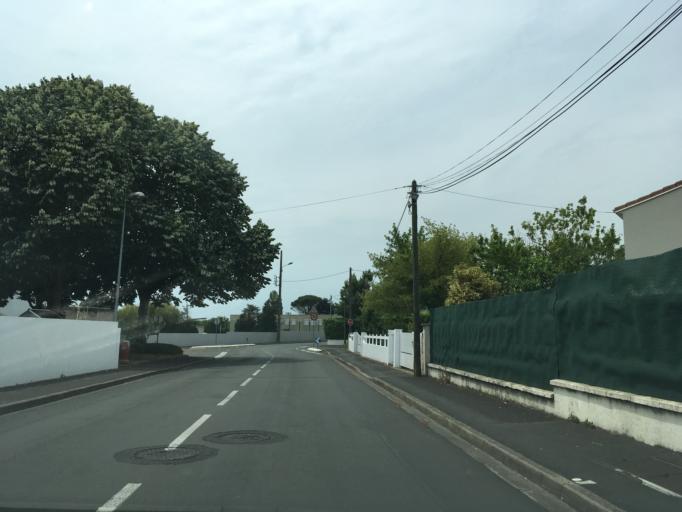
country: FR
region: Poitou-Charentes
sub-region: Departement des Deux-Sevres
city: Niort
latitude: 46.3189
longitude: -0.4765
